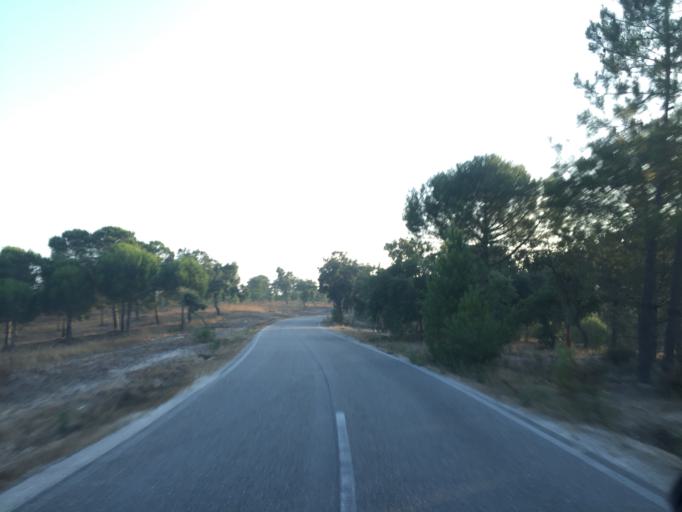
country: PT
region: Santarem
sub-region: Coruche
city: Coruche
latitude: 39.0373
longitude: -8.4432
